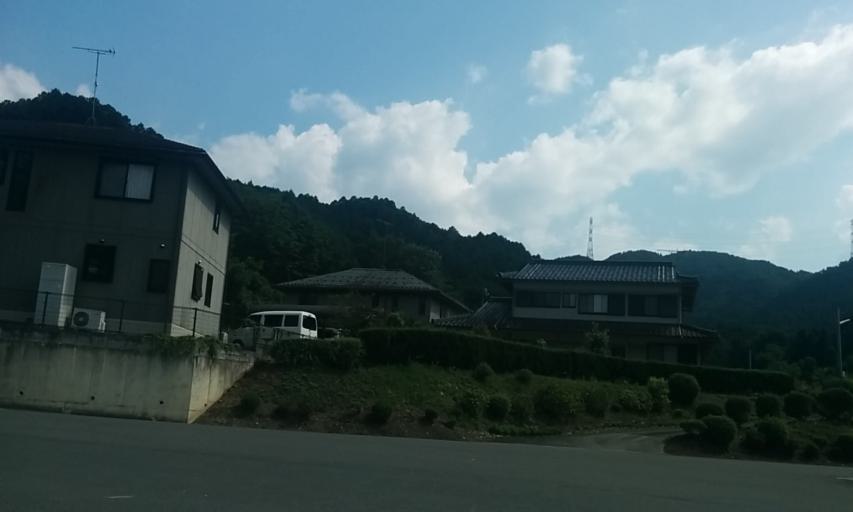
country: JP
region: Kyoto
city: Fukuchiyama
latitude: 35.3659
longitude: 135.1258
